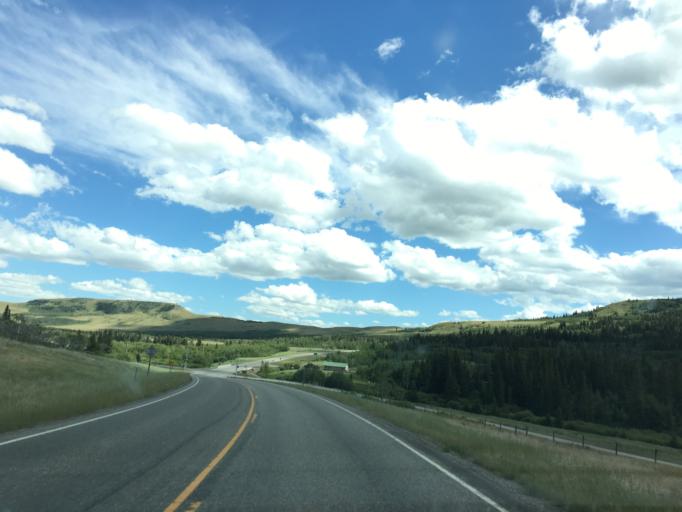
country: US
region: Montana
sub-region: Glacier County
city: Browning
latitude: 48.6107
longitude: -113.2899
